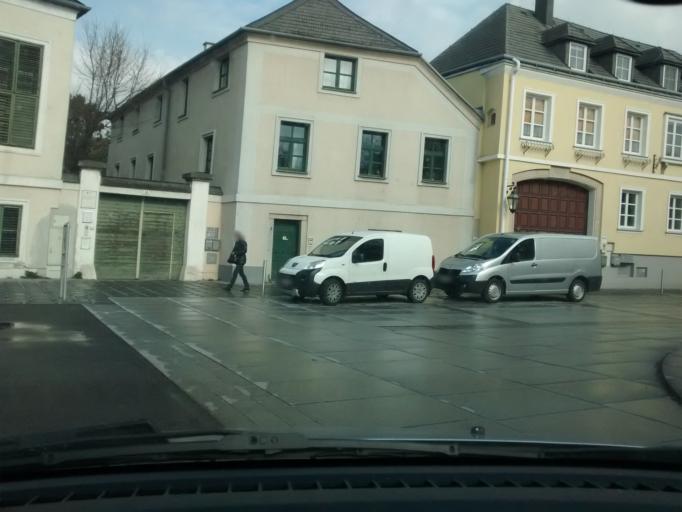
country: AT
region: Lower Austria
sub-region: Politischer Bezirk Modling
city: Laxenburg
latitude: 48.0672
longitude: 16.3563
